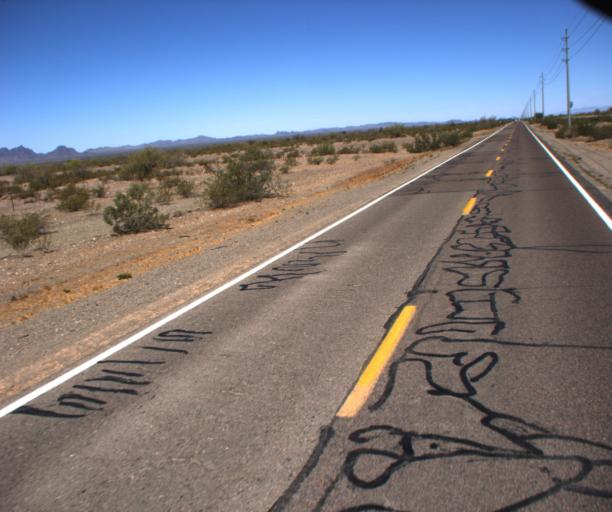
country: US
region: Arizona
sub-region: La Paz County
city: Salome
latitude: 33.7852
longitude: -113.8129
